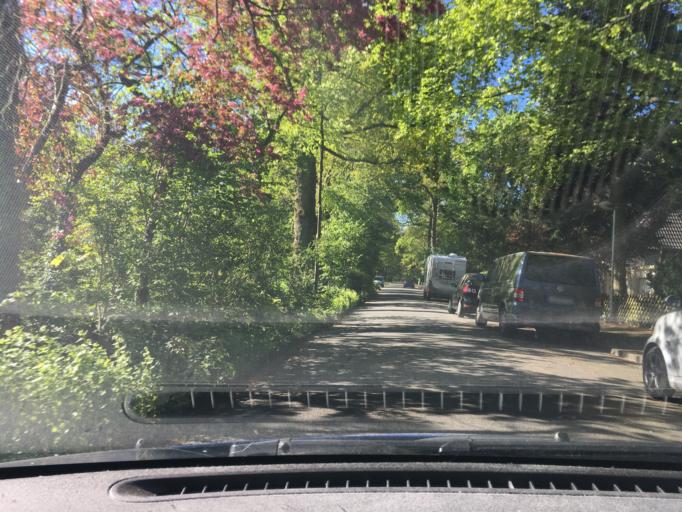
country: DE
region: Lower Saxony
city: Lueneburg
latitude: 53.2298
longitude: 10.4218
